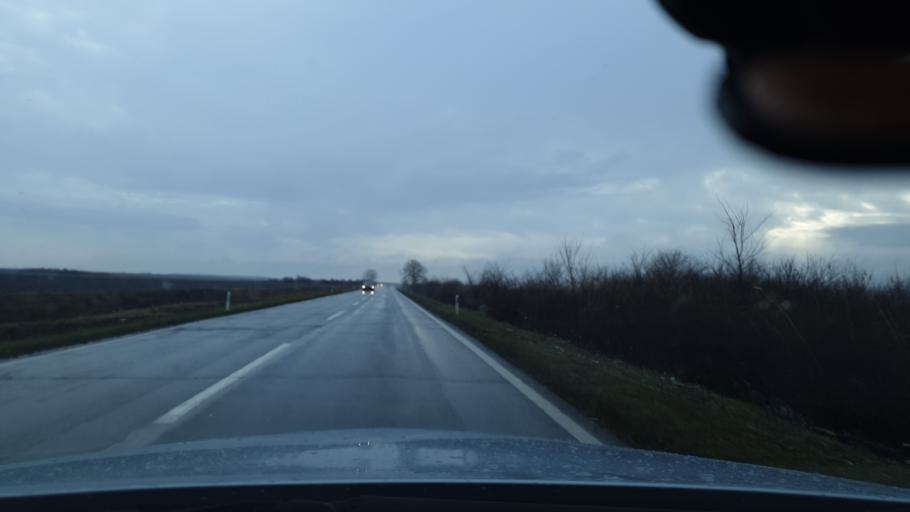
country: RS
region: Autonomna Pokrajina Vojvodina
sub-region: Juznobanatski Okrug
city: Pancevo
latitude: 44.8404
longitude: 20.8001
